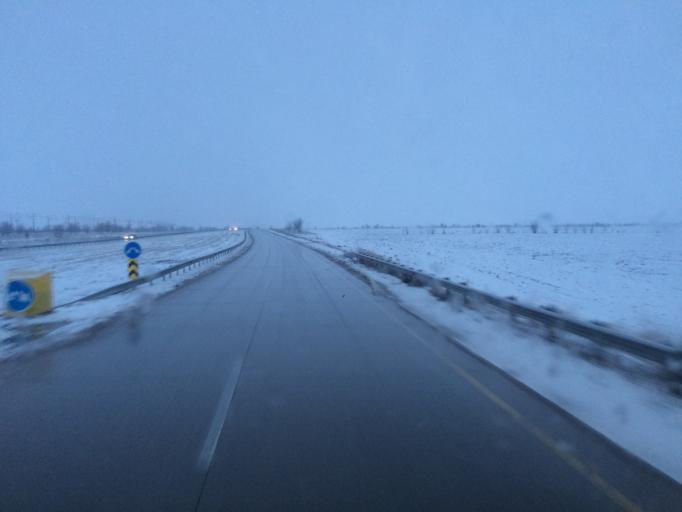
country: KZ
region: Zhambyl
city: Kulan
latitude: 42.9930
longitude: 72.3033
